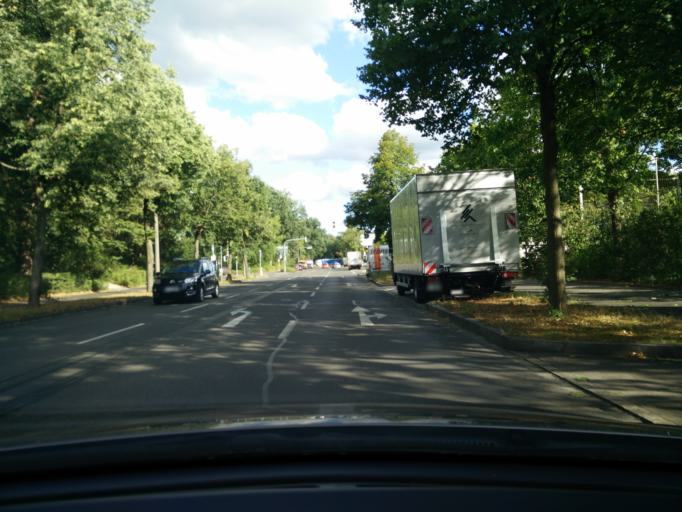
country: DE
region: Bavaria
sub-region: Regierungsbezirk Mittelfranken
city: Wendelstein
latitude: 49.3989
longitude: 11.1410
